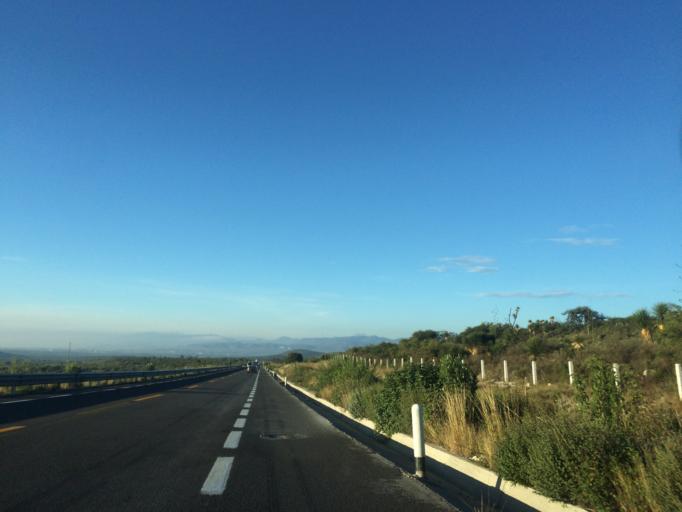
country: MX
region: Puebla
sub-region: Tehuacan
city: Magdalena Cuayucatepec
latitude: 18.6117
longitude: -97.4758
